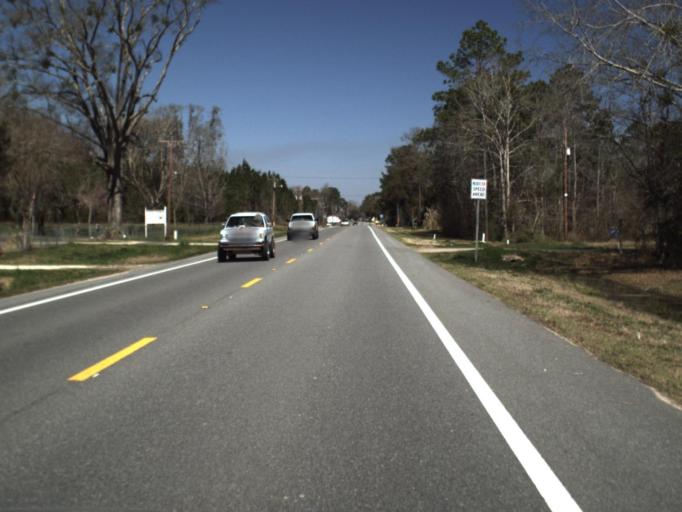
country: US
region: Florida
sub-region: Jackson County
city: Sneads
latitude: 30.6992
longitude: -85.0203
